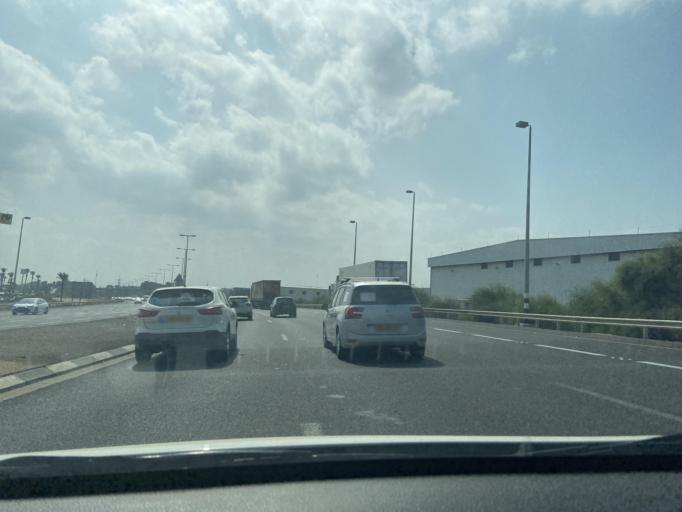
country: IL
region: Northern District
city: `Akko
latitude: 32.9033
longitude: 35.0901
